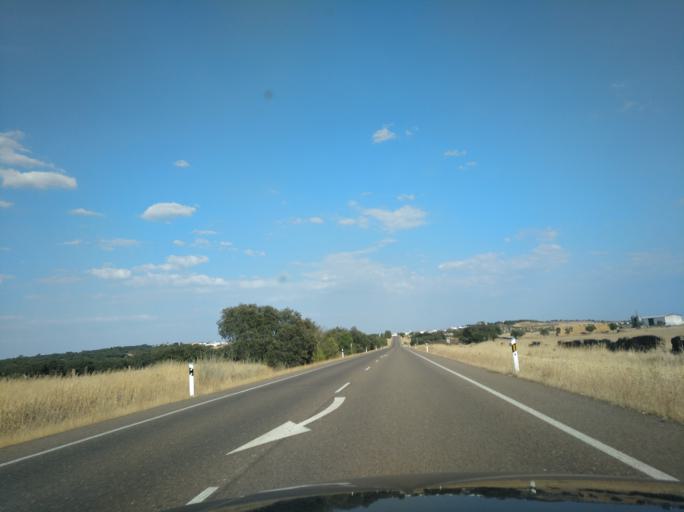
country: ES
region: Extremadura
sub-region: Provincia de Badajoz
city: Villanueva del Fresno
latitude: 38.3782
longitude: -7.1890
